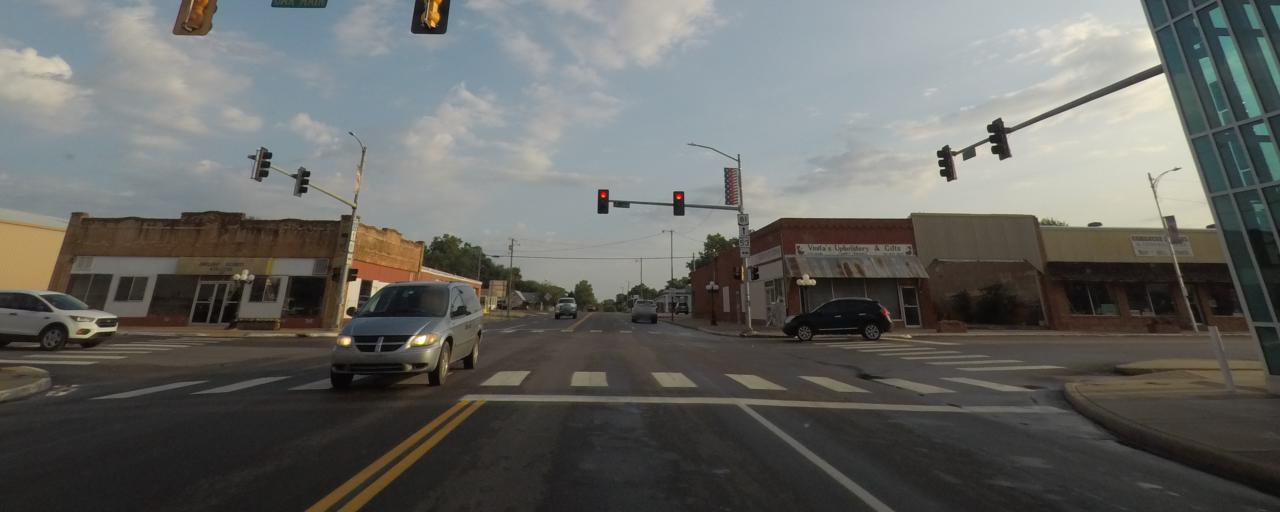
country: US
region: Oklahoma
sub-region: Stephens County
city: Comanche
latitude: 34.3688
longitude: -97.9642
